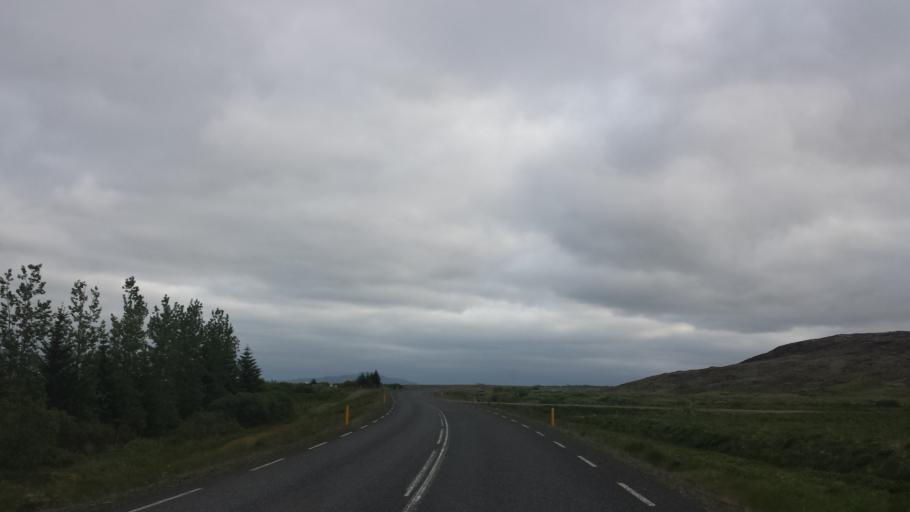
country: IS
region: South
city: Selfoss
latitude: 64.1384
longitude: -20.5732
